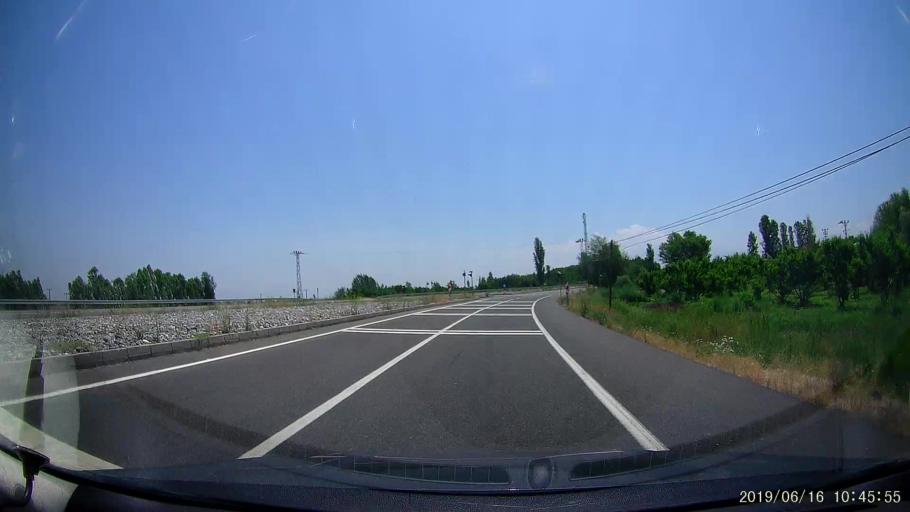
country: AM
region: Armavir
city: Shenavan
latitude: 40.0258
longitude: 43.8750
